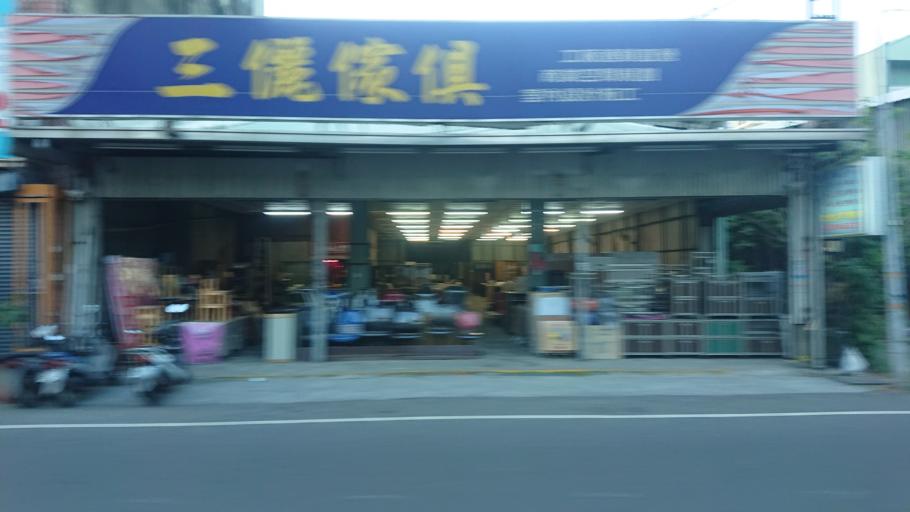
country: TW
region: Taiwan
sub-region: Tainan
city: Tainan
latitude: 23.0163
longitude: 120.2368
